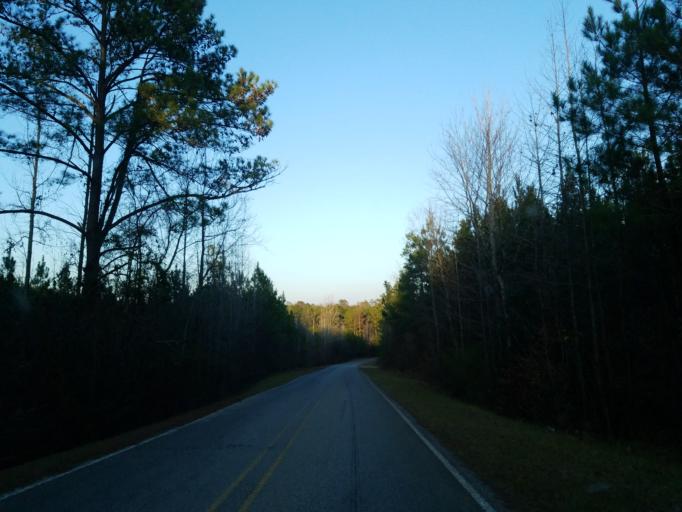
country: US
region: Mississippi
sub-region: Lauderdale County
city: Meridian
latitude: 32.2653
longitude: -88.7924
